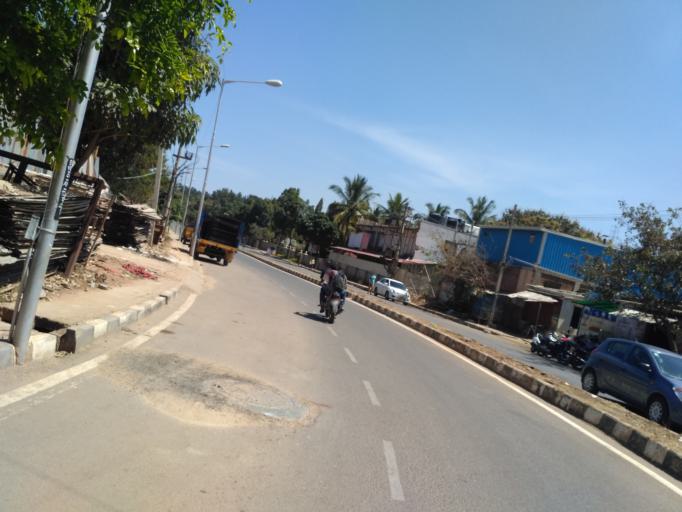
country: IN
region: Karnataka
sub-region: Bangalore Urban
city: Yelahanka
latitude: 13.0876
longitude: 77.5900
